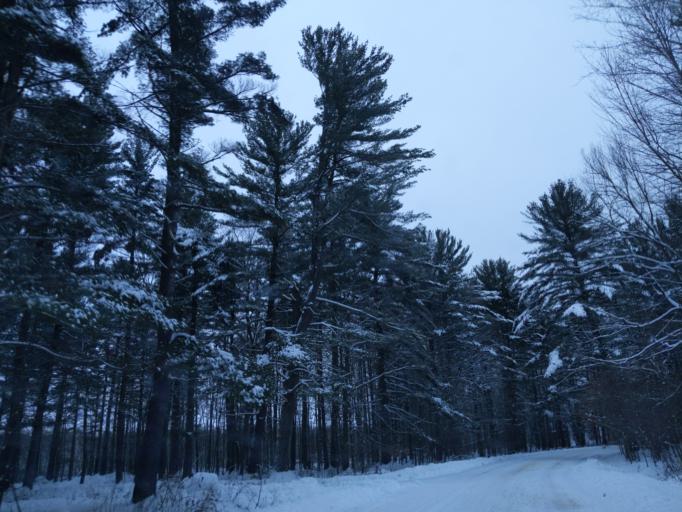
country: US
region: Wisconsin
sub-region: Marathon County
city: Marathon
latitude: 44.7703
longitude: -89.8694
